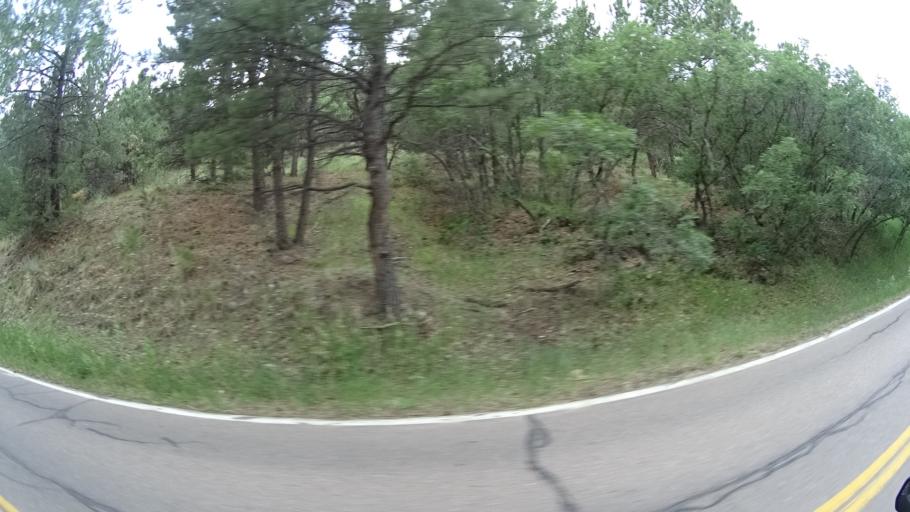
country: US
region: Colorado
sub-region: El Paso County
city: Colorado Springs
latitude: 38.9065
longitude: -104.8311
